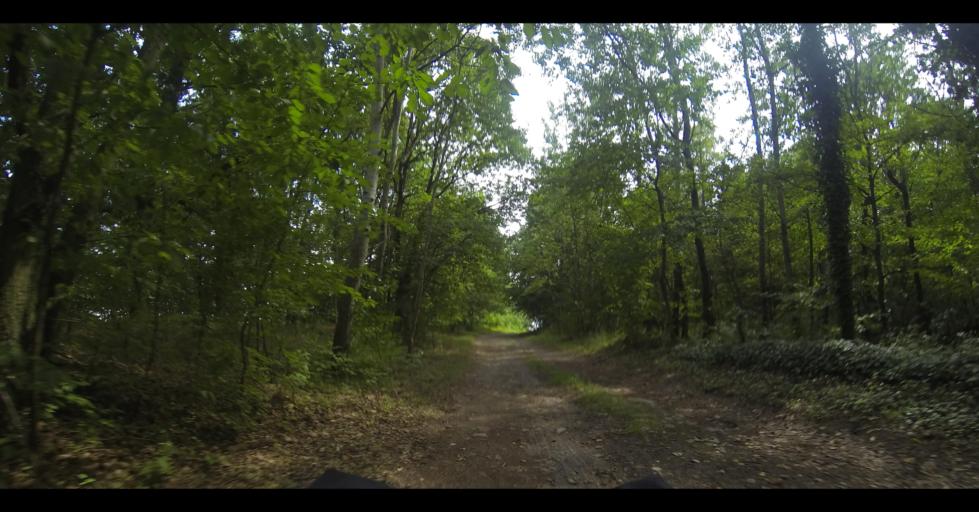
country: DE
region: Saxony
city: Moritzburg
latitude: 51.1334
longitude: 13.7140
